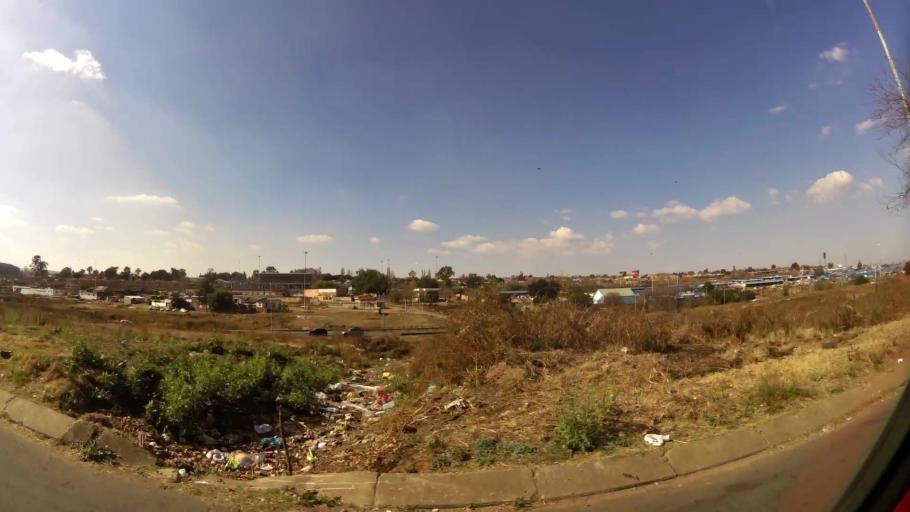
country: ZA
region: Gauteng
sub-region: City of Johannesburg Metropolitan Municipality
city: Soweto
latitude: -26.2368
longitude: 27.9133
